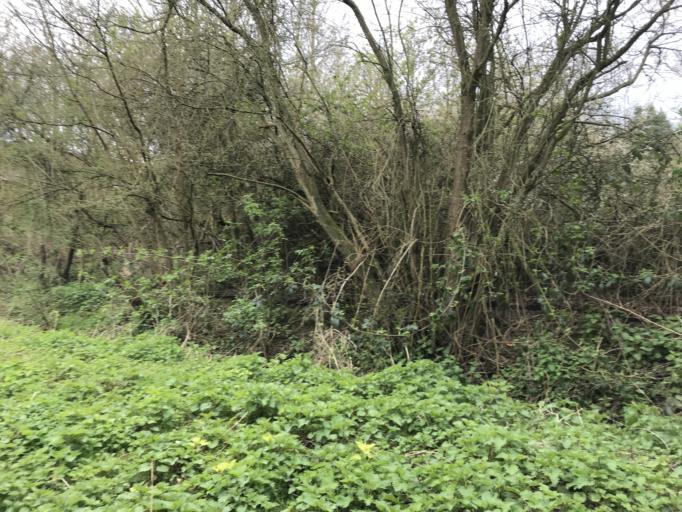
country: GB
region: England
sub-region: Essex
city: Stock
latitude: 51.6733
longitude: 0.4688
